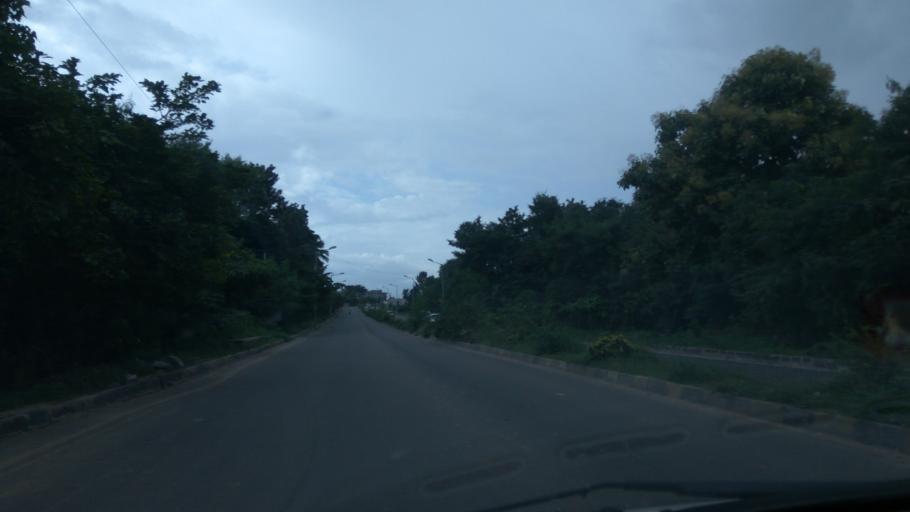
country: IN
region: Karnataka
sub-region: Bangalore Urban
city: Yelahanka
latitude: 13.1052
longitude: 77.6341
